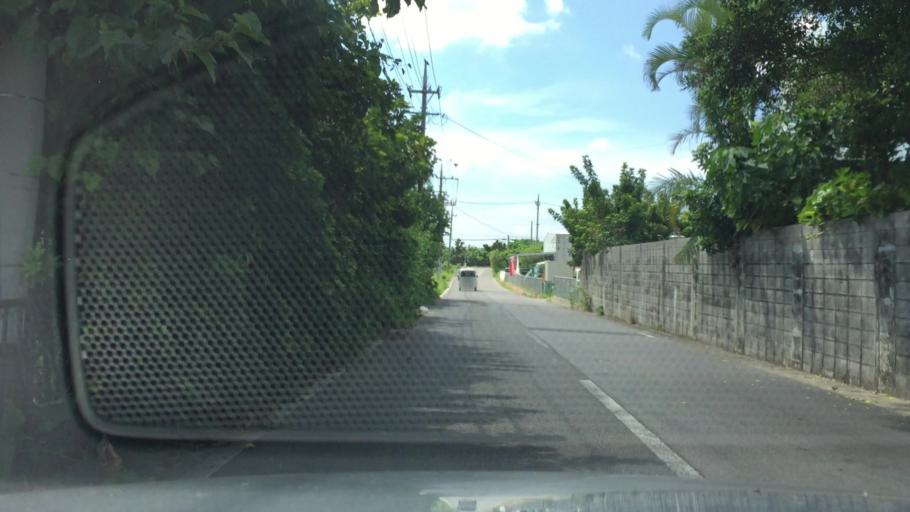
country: JP
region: Okinawa
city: Ishigaki
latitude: 24.3568
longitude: 124.2016
